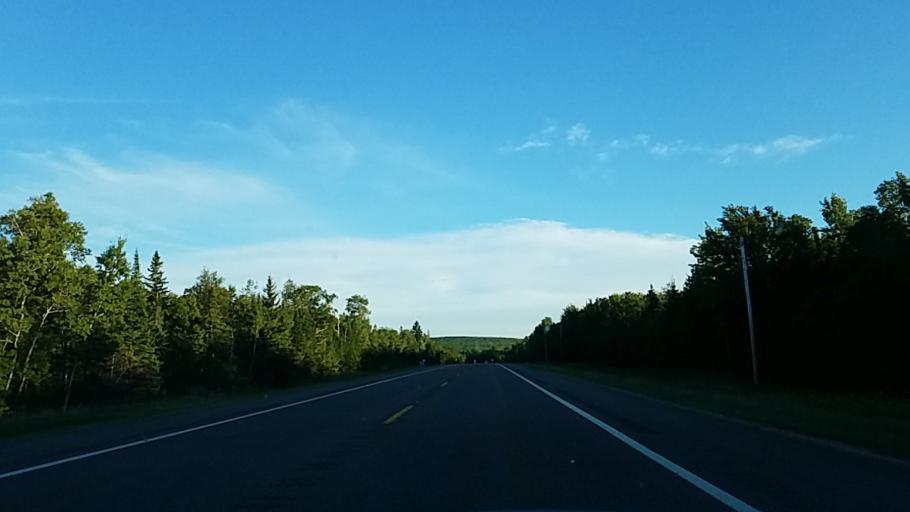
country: US
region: Michigan
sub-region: Alger County
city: Munising
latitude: 46.4512
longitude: -86.8887
